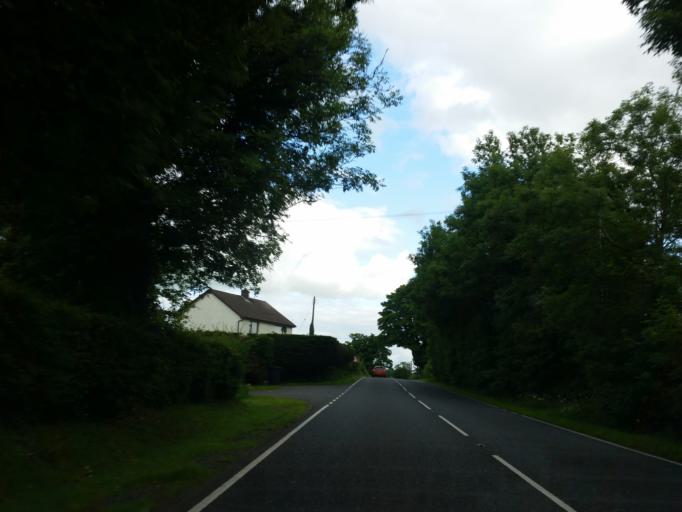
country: GB
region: Northern Ireland
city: Lisnaskea
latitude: 54.2683
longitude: -7.4635
